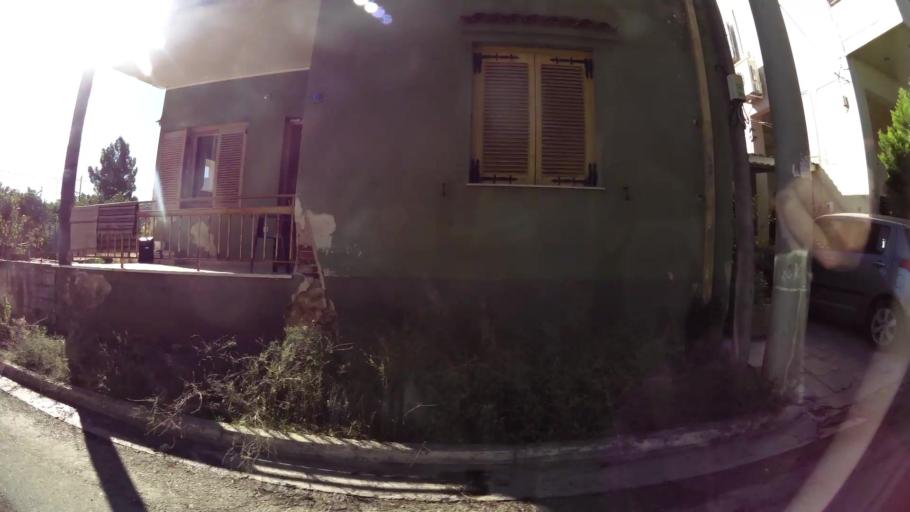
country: GR
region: Attica
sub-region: Nomarchia Anatolikis Attikis
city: Koropi
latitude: 37.8965
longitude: 23.8633
